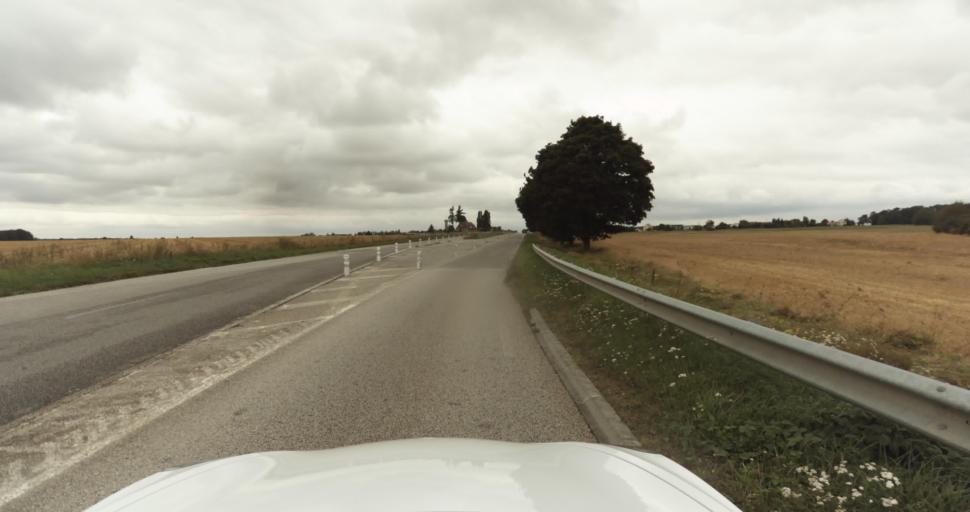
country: FR
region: Haute-Normandie
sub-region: Departement de l'Eure
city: Aviron
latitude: 49.0283
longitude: 1.1054
